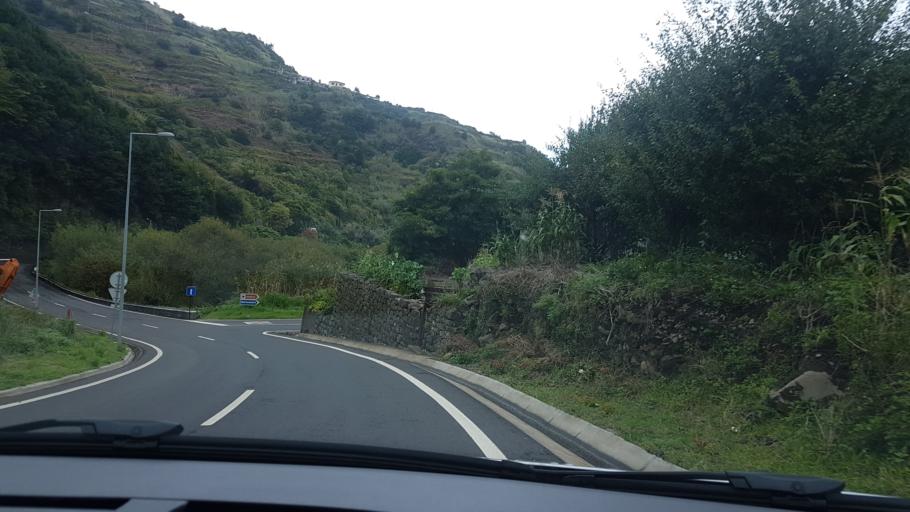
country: PT
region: Madeira
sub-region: Sao Vicente
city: Sao Vicente
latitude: 32.8208
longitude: -16.9756
